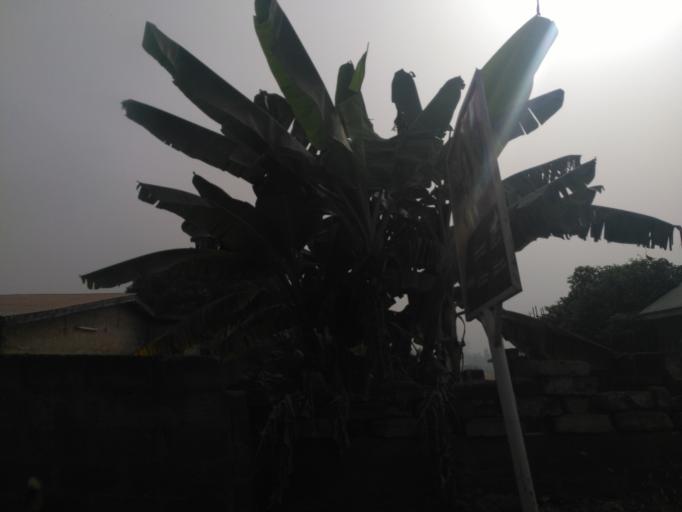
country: GH
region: Ashanti
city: Kumasi
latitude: 6.6650
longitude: -1.6137
